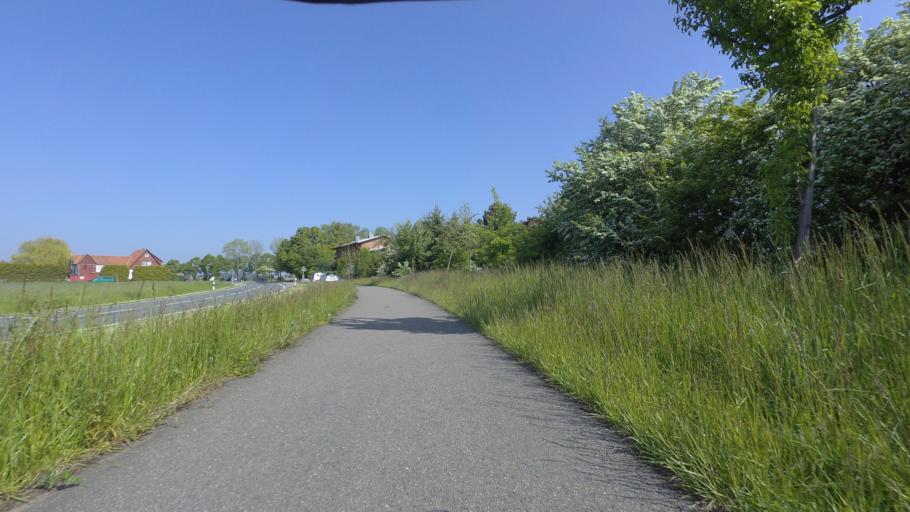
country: DE
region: Saxony-Anhalt
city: Darlingerode
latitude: 51.8528
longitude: 10.7284
